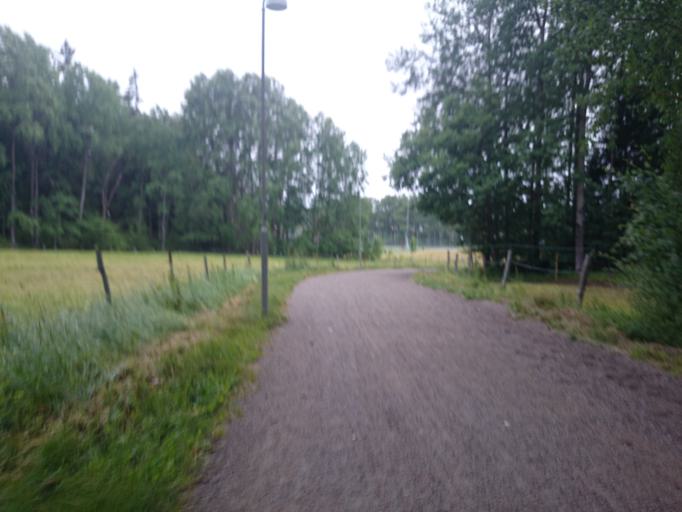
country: SE
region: Stockholm
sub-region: Huddinge Kommun
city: Segeltorp
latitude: 59.2667
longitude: 17.9330
